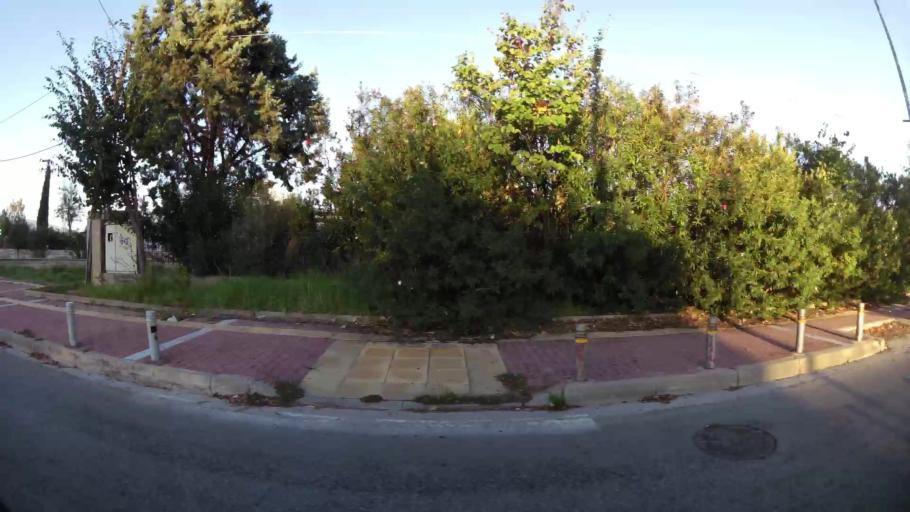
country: GR
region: Attica
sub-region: Nomarchia Anatolikis Attikis
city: Spata
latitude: 37.9695
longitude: 23.9057
